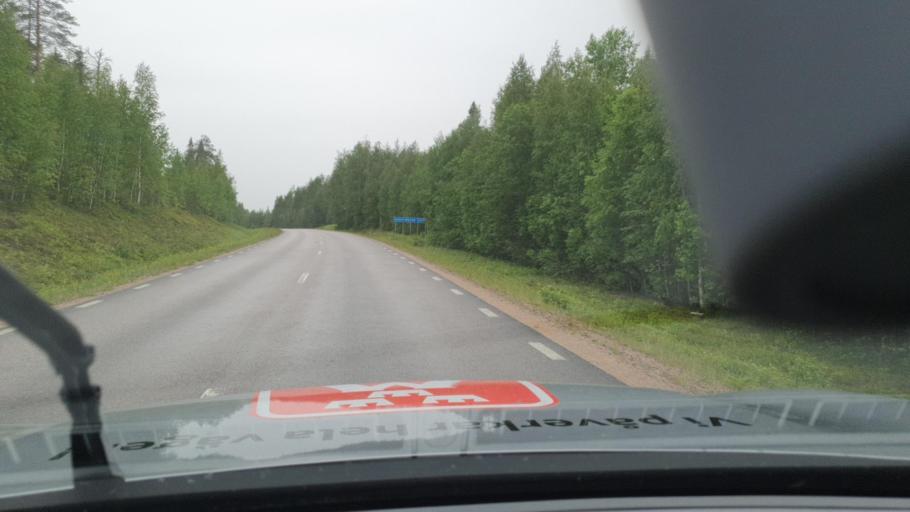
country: SE
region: Norrbotten
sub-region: Overtornea Kommun
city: OEvertornea
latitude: 66.4218
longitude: 23.3793
